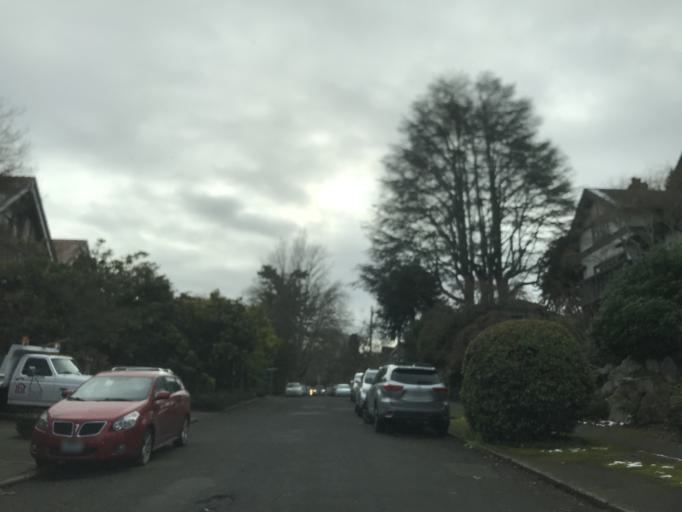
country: US
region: Washington
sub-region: King County
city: Seattle
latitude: 47.6311
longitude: -122.3036
